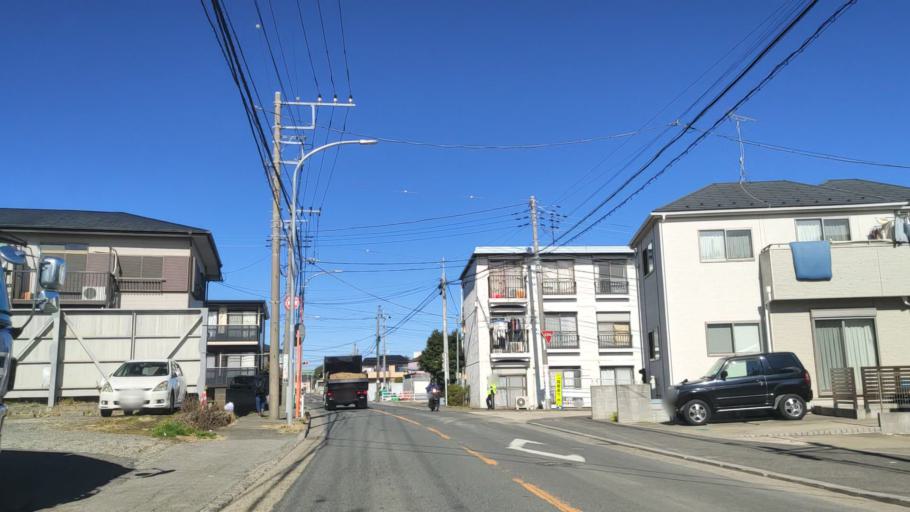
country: JP
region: Kanagawa
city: Minami-rinkan
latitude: 35.4946
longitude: 139.5167
